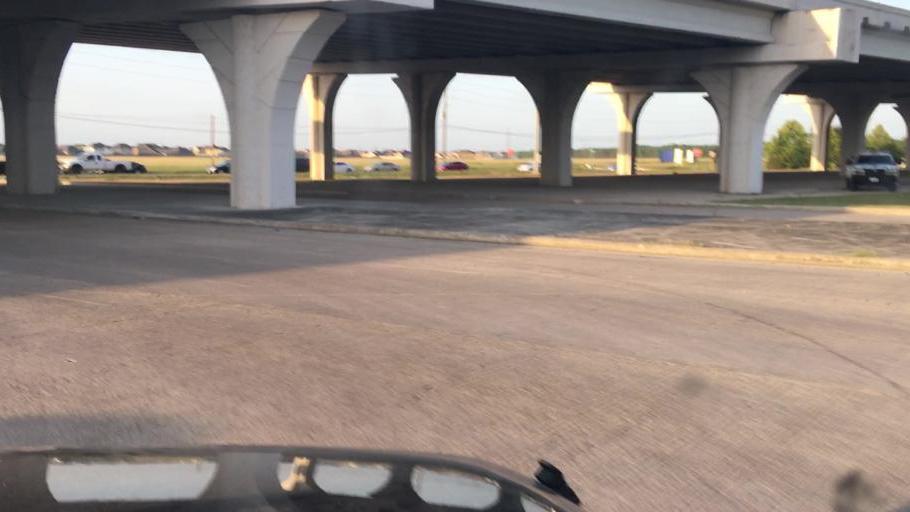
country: US
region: Texas
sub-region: Harris County
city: Atascocita
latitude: 29.9339
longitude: -95.2114
